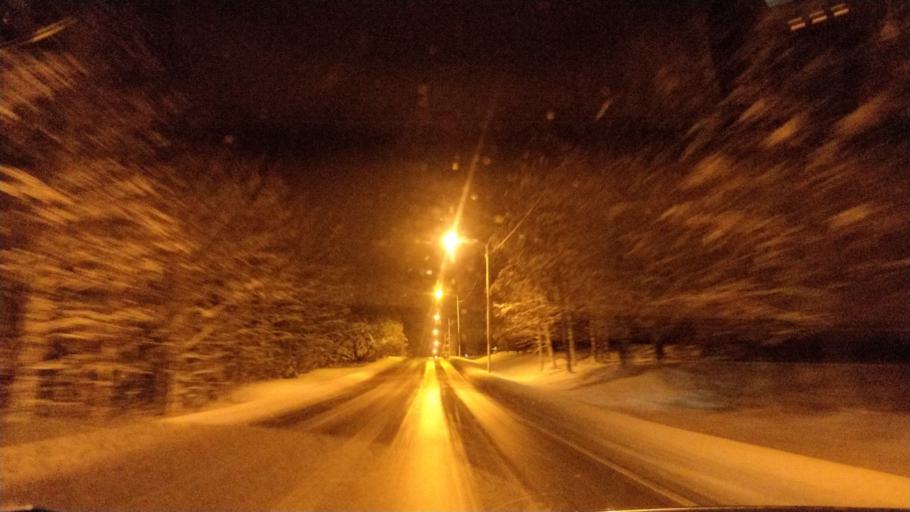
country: FI
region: Lapland
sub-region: Rovaniemi
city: Rovaniemi
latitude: 66.2999
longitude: 25.3533
